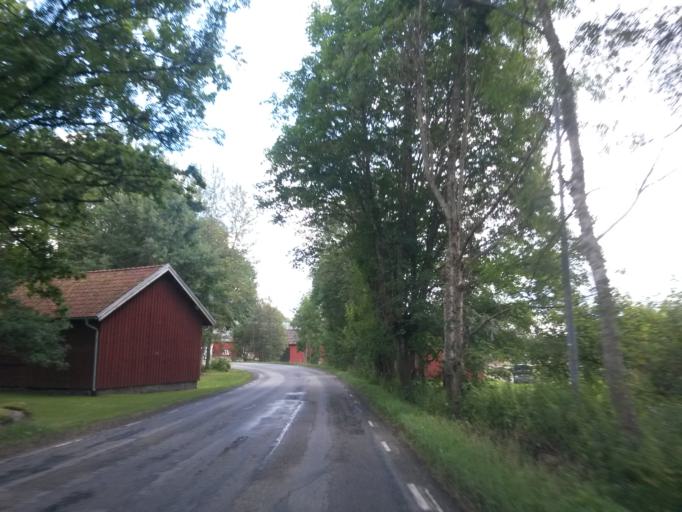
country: SE
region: Vaestra Goetaland
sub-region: Herrljunga Kommun
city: Herrljunga
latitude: 58.0170
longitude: 13.0462
